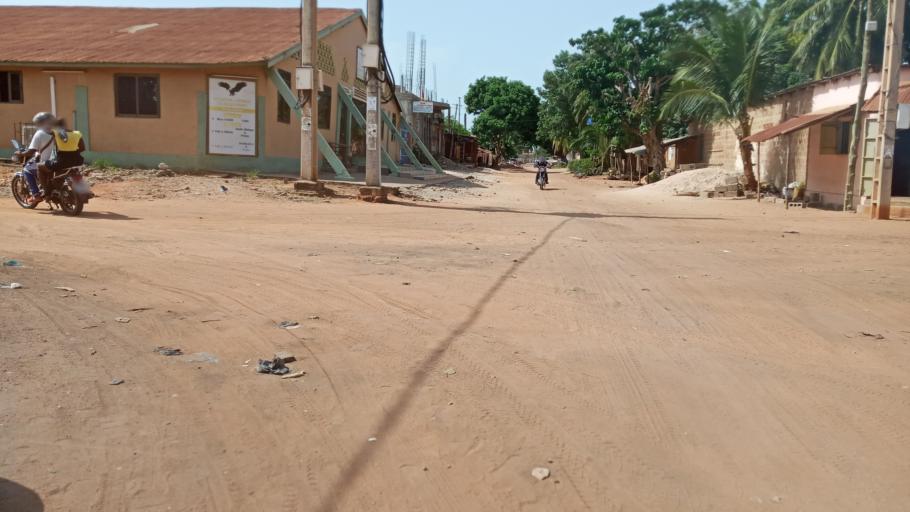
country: TG
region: Maritime
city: Lome
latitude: 6.2073
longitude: 1.1841
